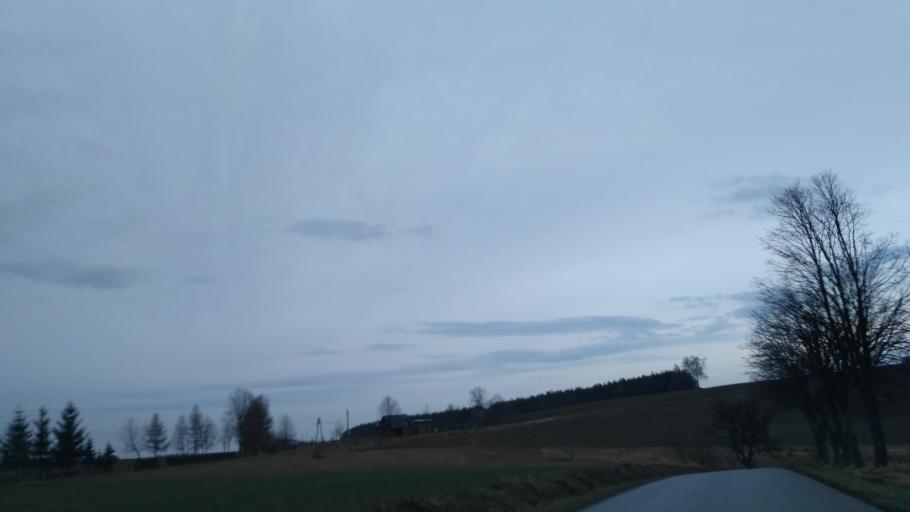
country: PL
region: Subcarpathian Voivodeship
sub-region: Powiat strzyzowski
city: Polomia
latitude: 49.8757
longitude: 21.8584
